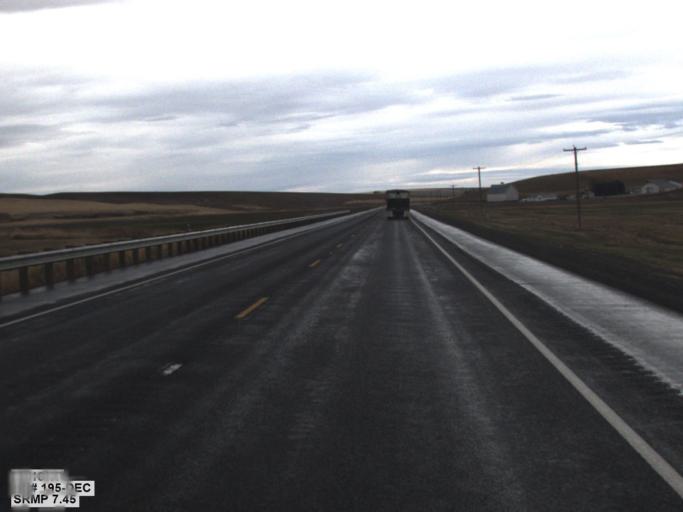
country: US
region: Washington
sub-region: Asotin County
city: Clarkston
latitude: 46.5648
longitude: -117.1140
